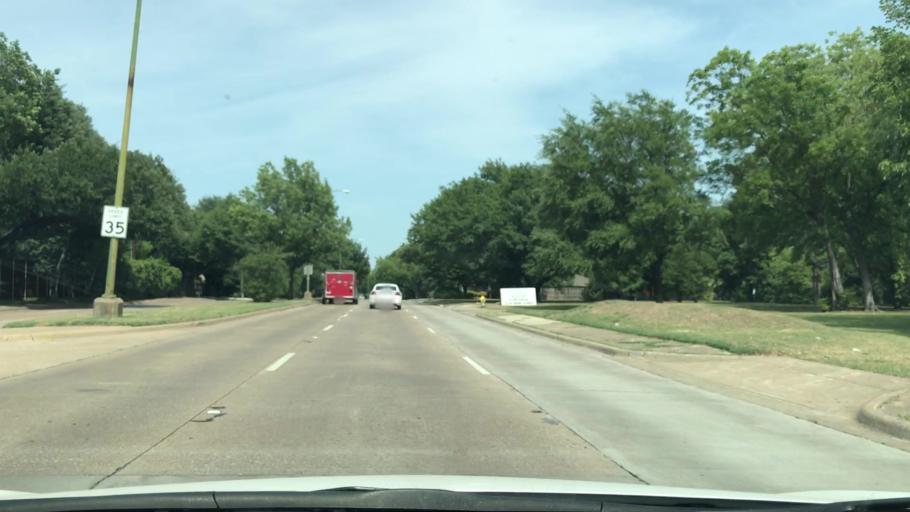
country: US
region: Texas
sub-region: Dallas County
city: University Park
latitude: 32.8800
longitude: -96.8024
